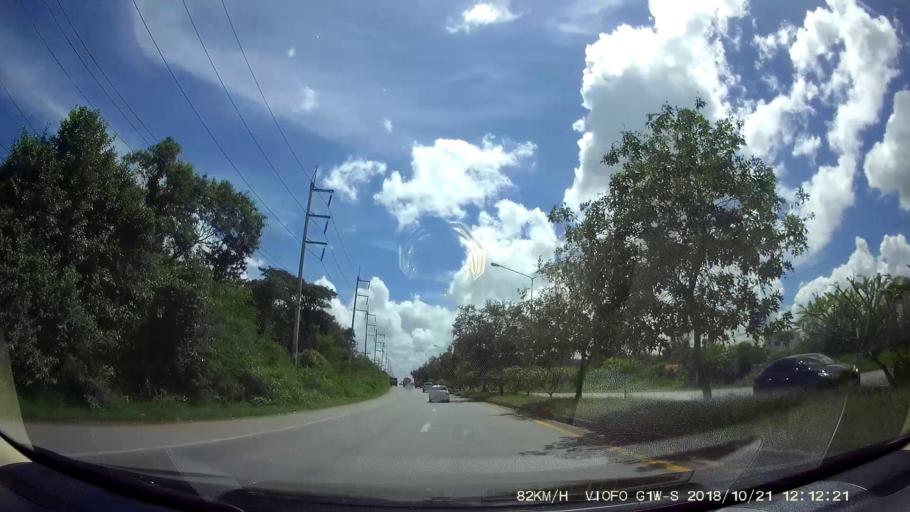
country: TH
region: Chaiyaphum
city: Chatturat
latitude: 15.4078
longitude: 101.8346
